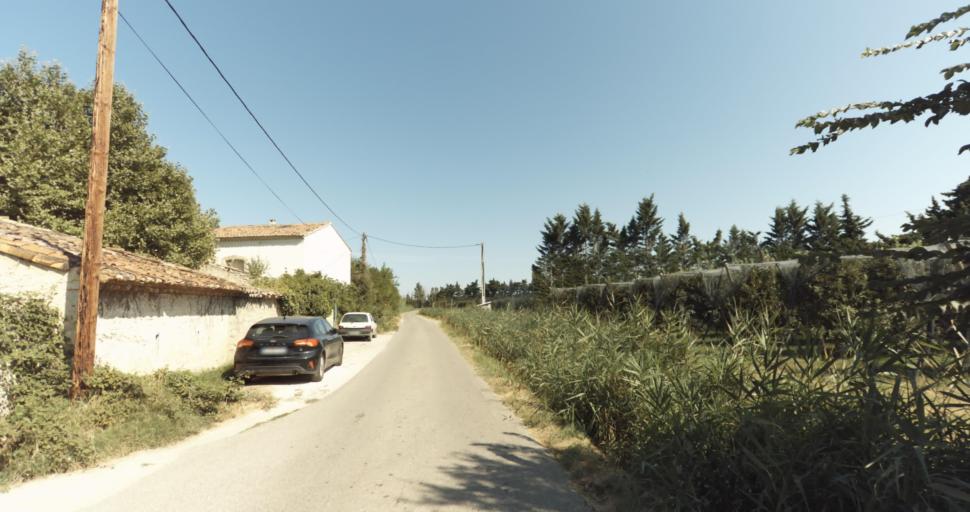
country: FR
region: Provence-Alpes-Cote d'Azur
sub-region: Departement du Vaucluse
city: Althen-des-Paluds
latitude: 44.0011
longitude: 4.9900
